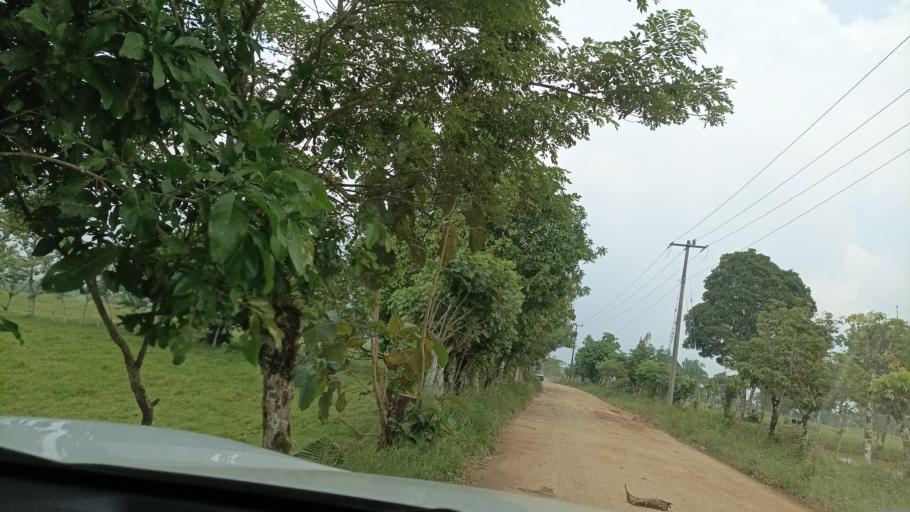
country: MX
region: Tabasco
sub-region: Huimanguillo
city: Francisco Rueda
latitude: 17.5921
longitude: -94.1987
